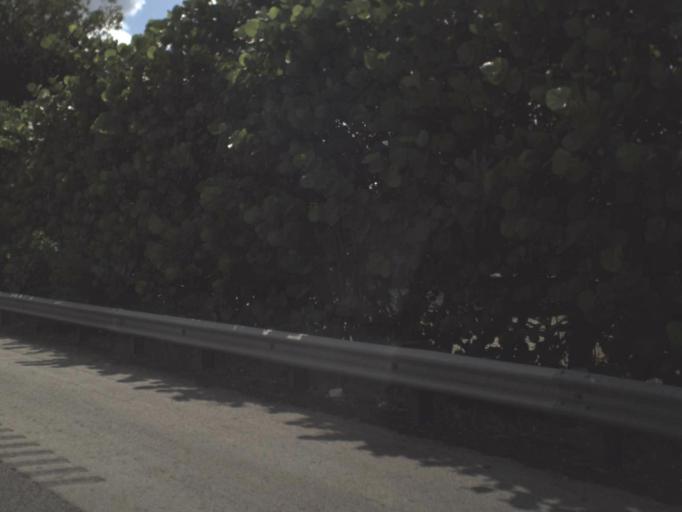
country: US
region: Florida
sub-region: Broward County
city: Davie
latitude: 26.0493
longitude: -80.2149
